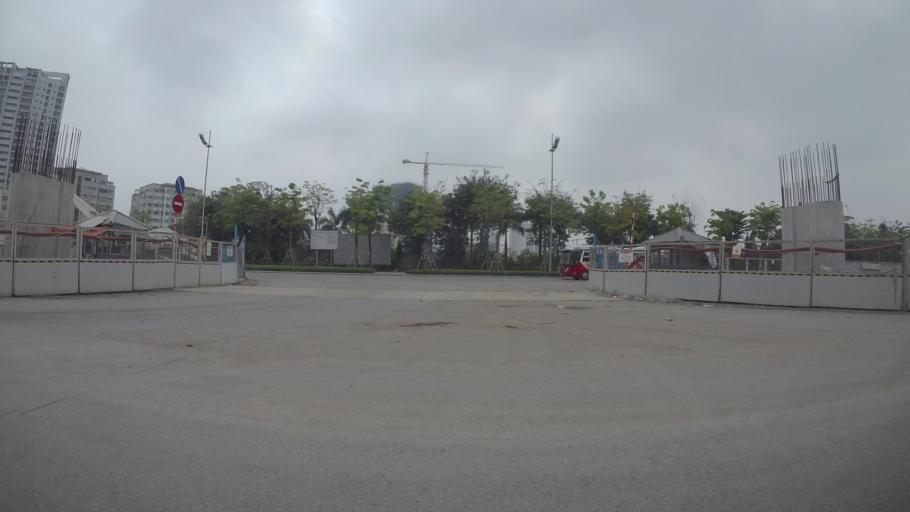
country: VN
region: Ha Noi
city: Tay Ho
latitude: 21.0671
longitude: 105.7849
